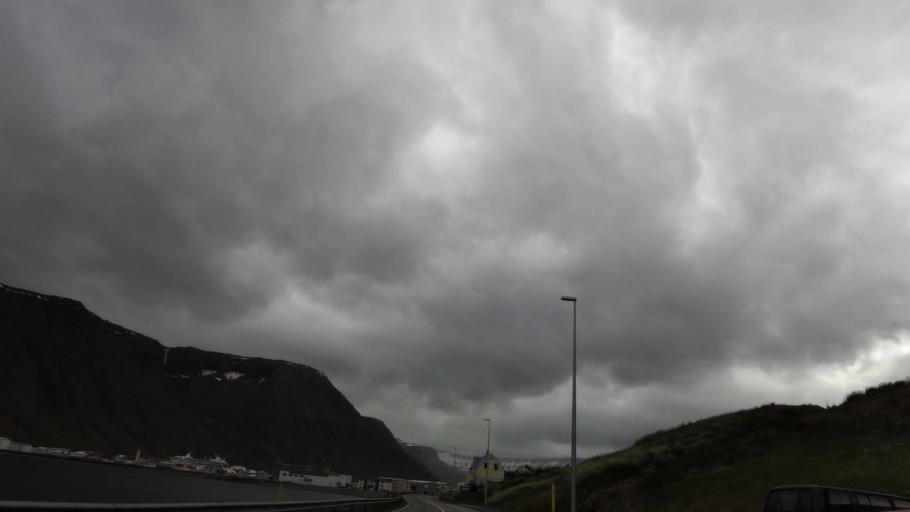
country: IS
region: Westfjords
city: Isafjoerdur
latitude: 66.0816
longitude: -23.1234
